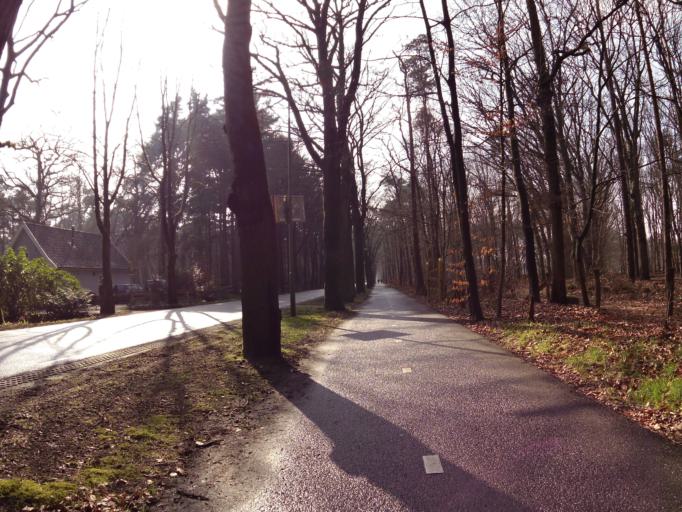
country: NL
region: North Brabant
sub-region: Gemeente Sint-Michielsgestel
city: Sint-Michielsgestel
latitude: 51.6247
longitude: 5.3307
